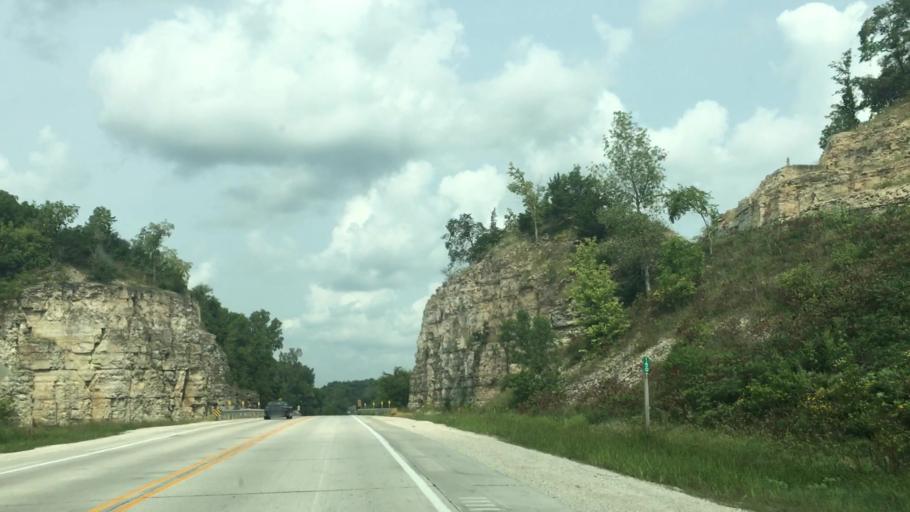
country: US
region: Iowa
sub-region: Winneshiek County
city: Decorah
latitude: 43.2947
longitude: -91.8078
